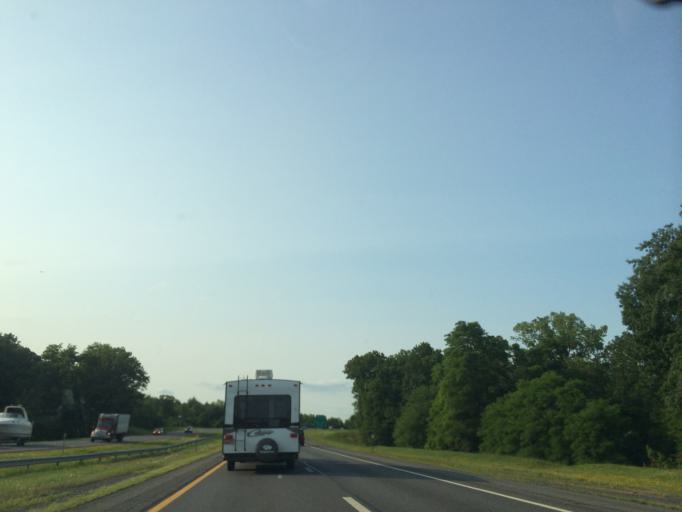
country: US
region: New York
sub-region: Albany County
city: Ravena
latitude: 42.4793
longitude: -73.8077
